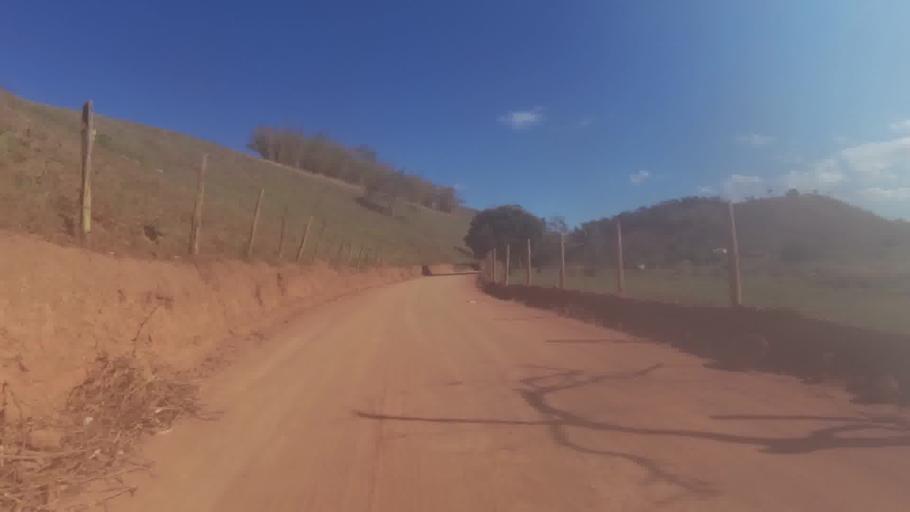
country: BR
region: Espirito Santo
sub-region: Cachoeiro De Itapemirim
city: Cachoeiro de Itapemirim
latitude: -21.0203
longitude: -41.0461
